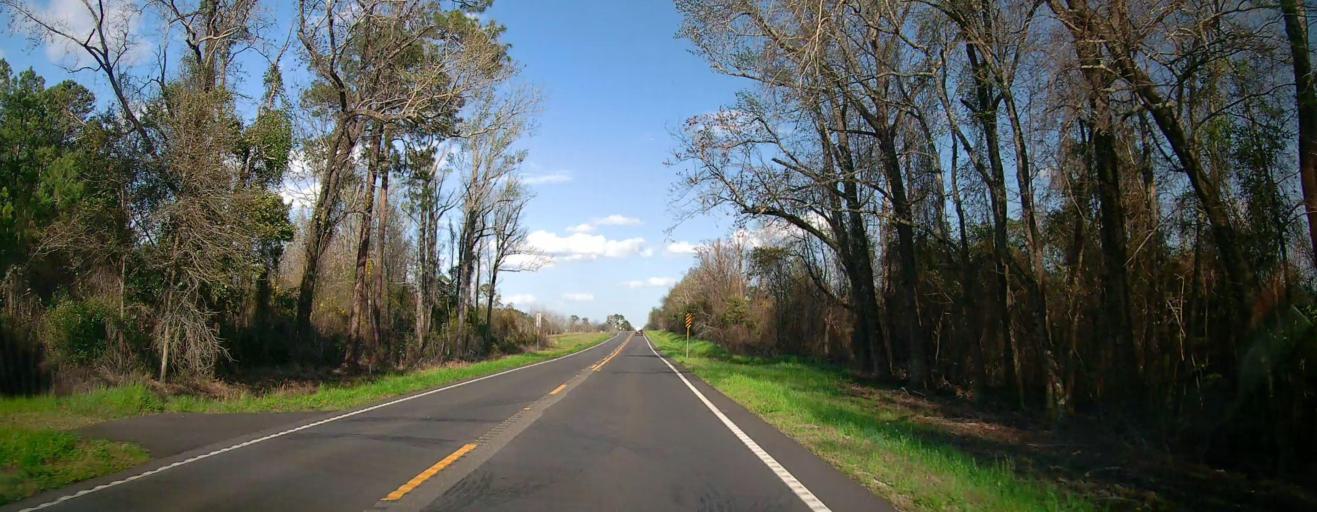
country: US
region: Georgia
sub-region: Montgomery County
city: Mount Vernon
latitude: 32.1858
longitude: -82.5352
